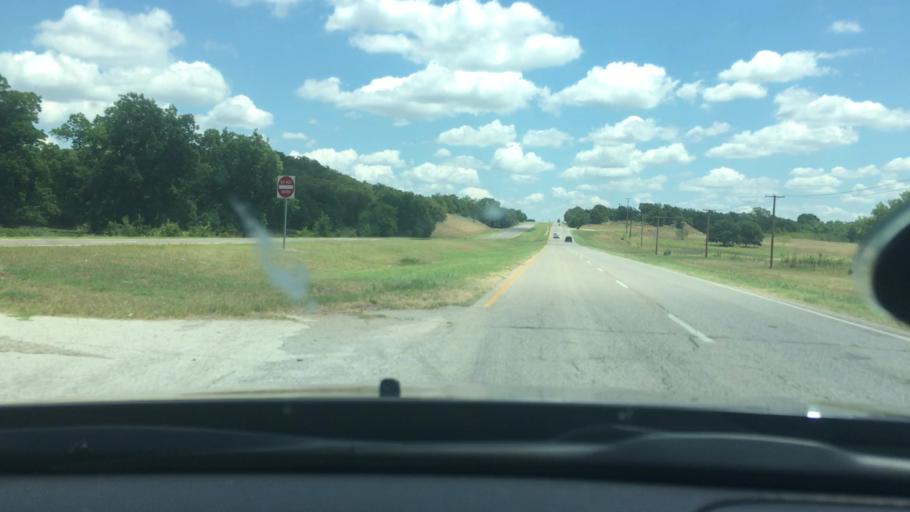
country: US
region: Oklahoma
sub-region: Carter County
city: Wilson
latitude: 34.1728
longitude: -97.3567
